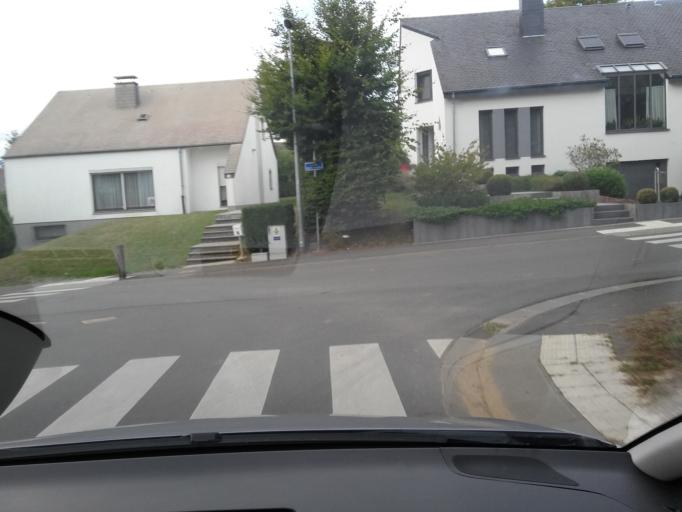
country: BE
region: Wallonia
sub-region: Province du Luxembourg
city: Arlon
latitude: 49.6904
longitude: 5.8017
